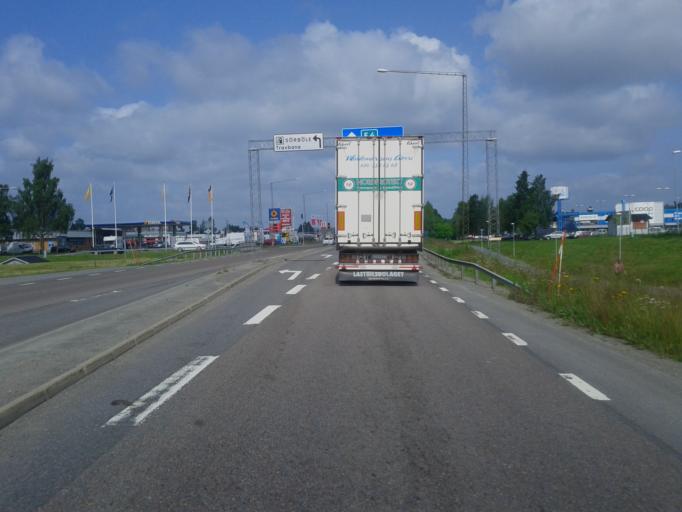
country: SE
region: Vaesterbotten
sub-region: Skelleftea Kommun
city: Skelleftea
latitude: 64.7362
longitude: 20.9670
